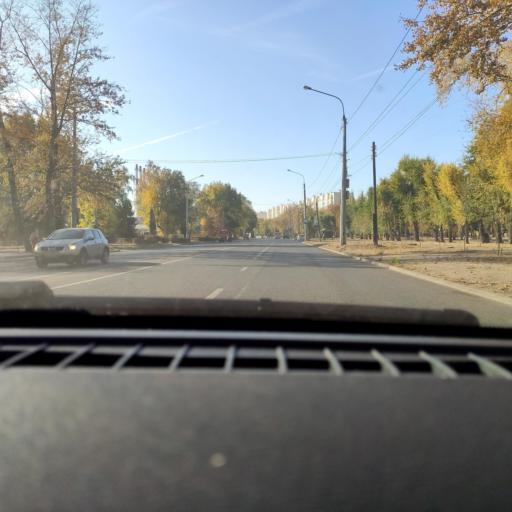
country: RU
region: Voronezj
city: Maslovka
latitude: 51.6079
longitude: 39.2446
